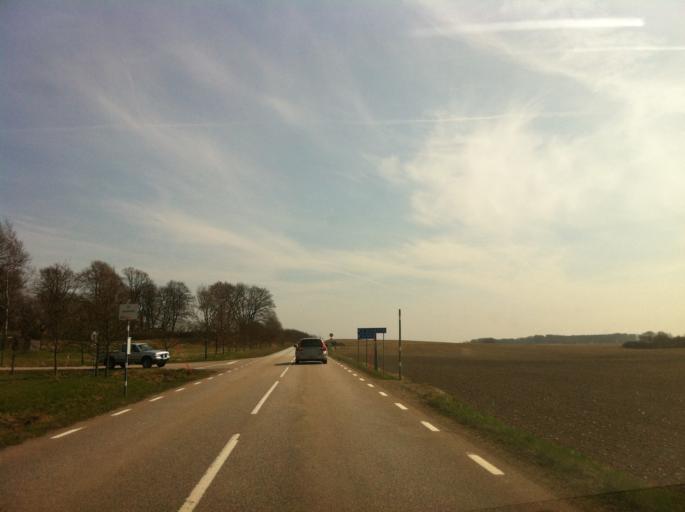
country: SE
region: Skane
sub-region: Klippans Kommun
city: Ljungbyhed
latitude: 55.9795
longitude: 13.1916
